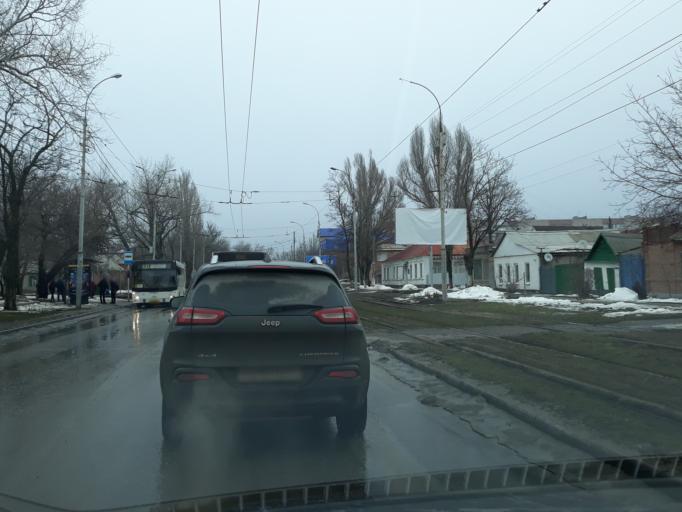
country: RU
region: Rostov
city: Taganrog
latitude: 47.2341
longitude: 38.9176
